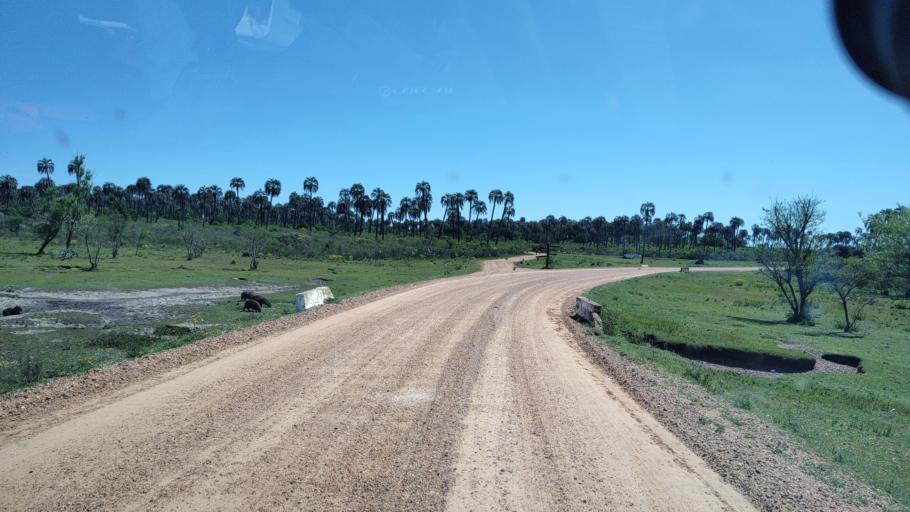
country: AR
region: Entre Rios
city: Ubajay
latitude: -31.8743
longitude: -58.2289
